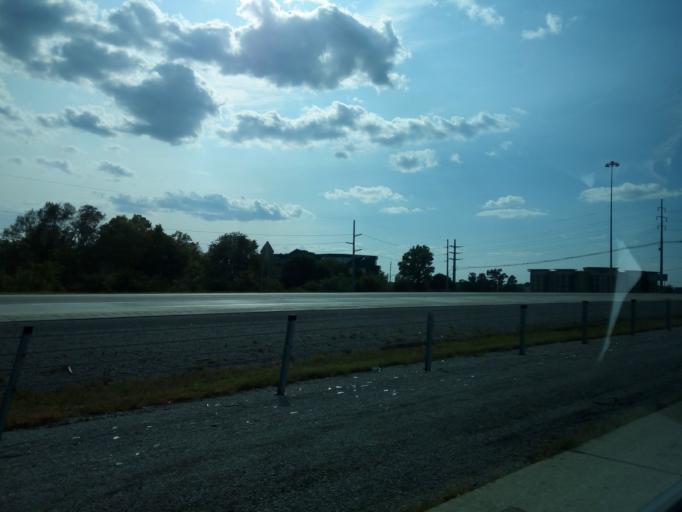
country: US
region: Kentucky
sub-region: Jefferson County
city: Worthington
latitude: 38.3084
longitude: -85.5702
